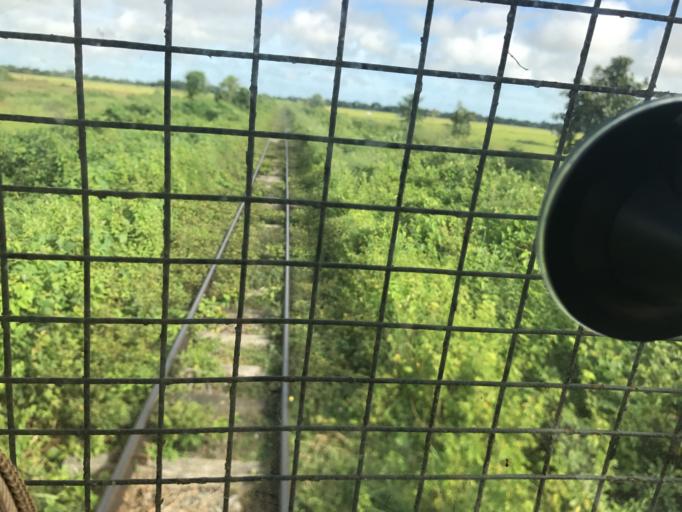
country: MM
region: Bago
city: Letpandan
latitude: 18.0074
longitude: 95.7016
